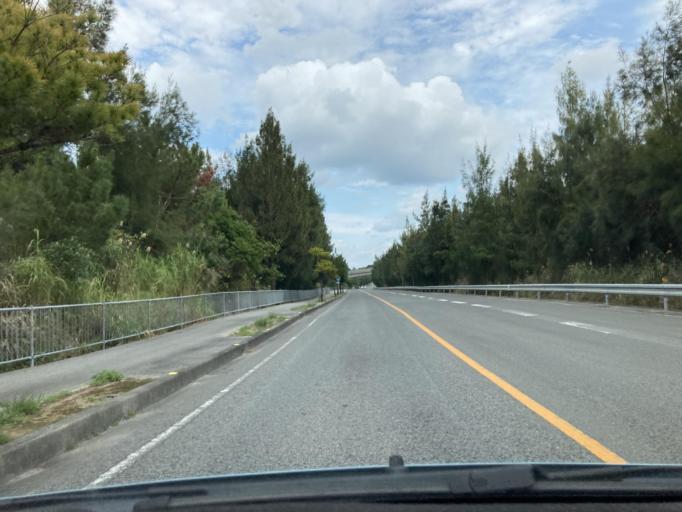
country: JP
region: Okinawa
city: Ishikawa
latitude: 26.4542
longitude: 127.8212
